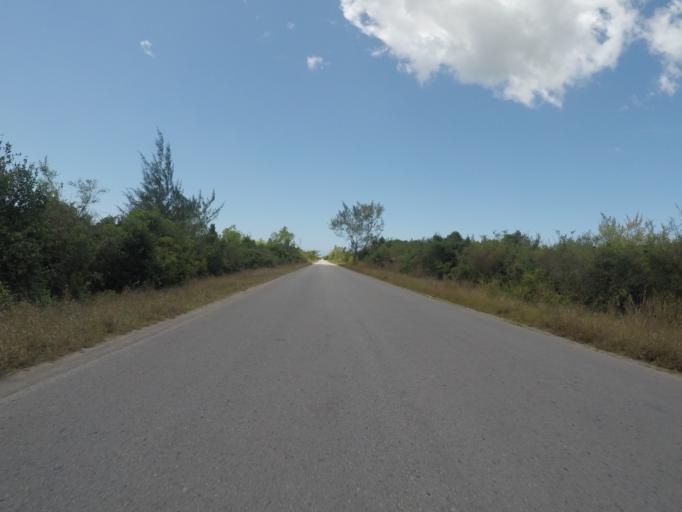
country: TZ
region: Zanzibar Central/South
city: Nganane
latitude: -6.2800
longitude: 39.4767
